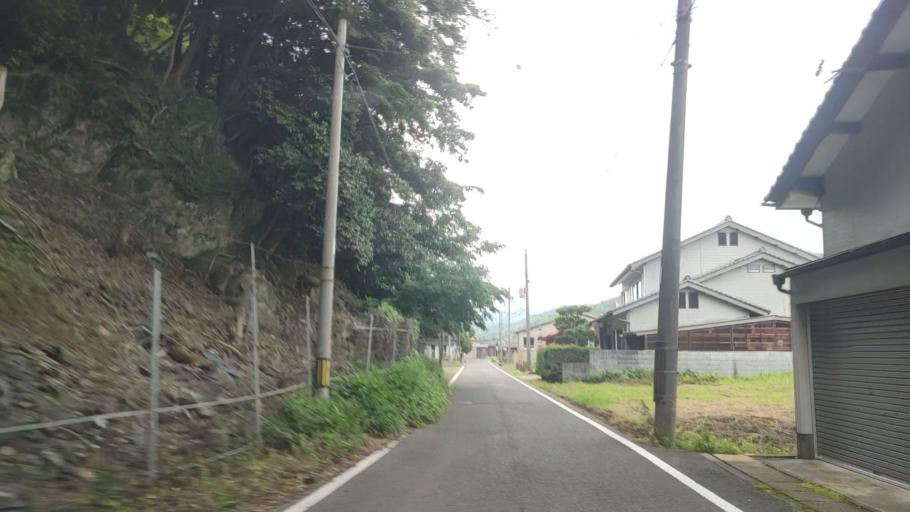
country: JP
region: Hyogo
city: Toyooka
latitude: 35.6402
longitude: 134.8402
